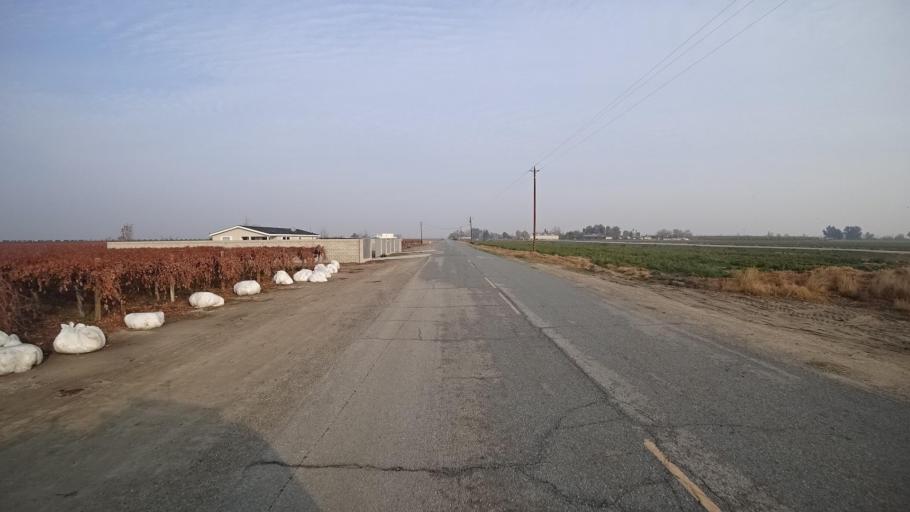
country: US
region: California
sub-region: Kern County
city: Greenfield
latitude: 35.2164
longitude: -119.0215
